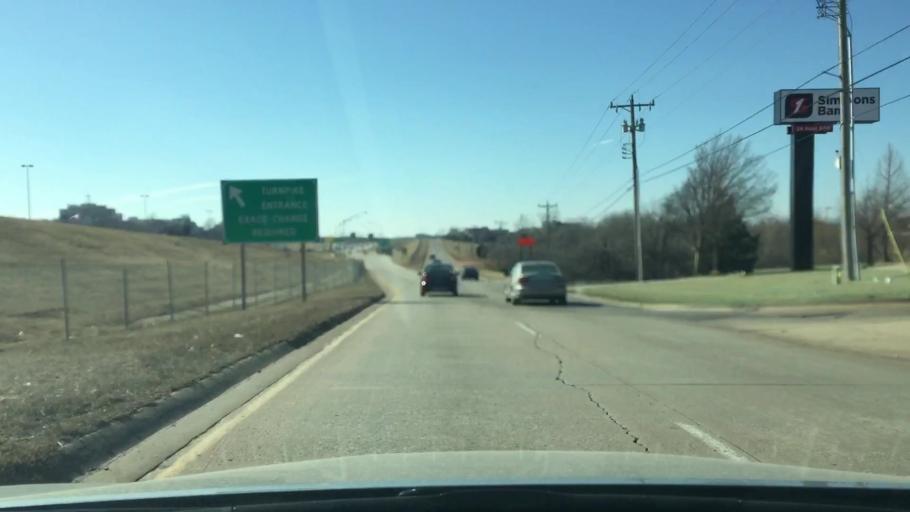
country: US
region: Oklahoma
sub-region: Oklahoma County
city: The Village
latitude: 35.6101
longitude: -97.5871
